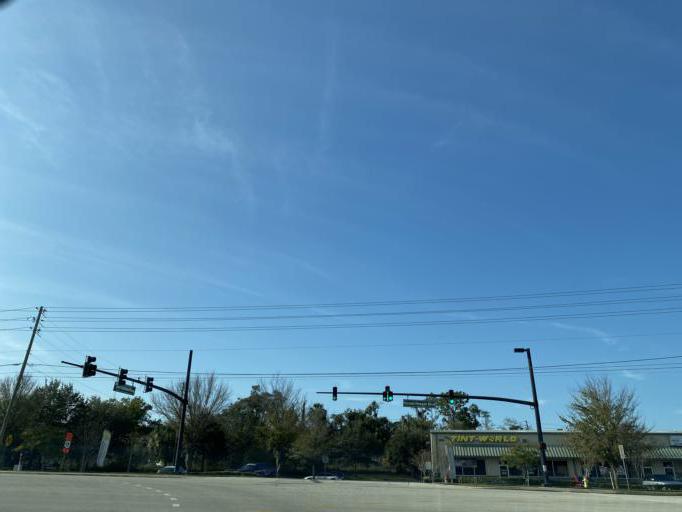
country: US
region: Florida
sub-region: Seminole County
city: Longwood
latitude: 28.7218
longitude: -81.3357
